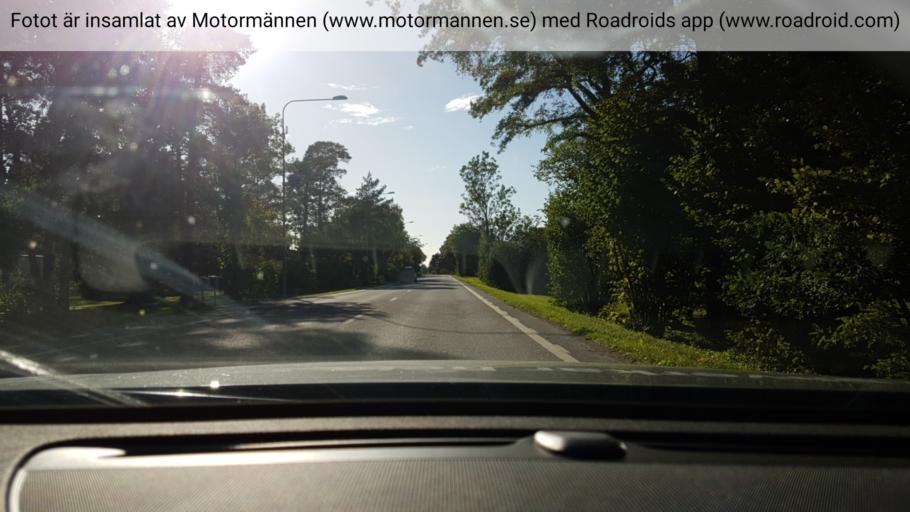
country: SE
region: Gotland
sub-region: Gotland
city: Hemse
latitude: 57.2469
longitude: 18.3955
